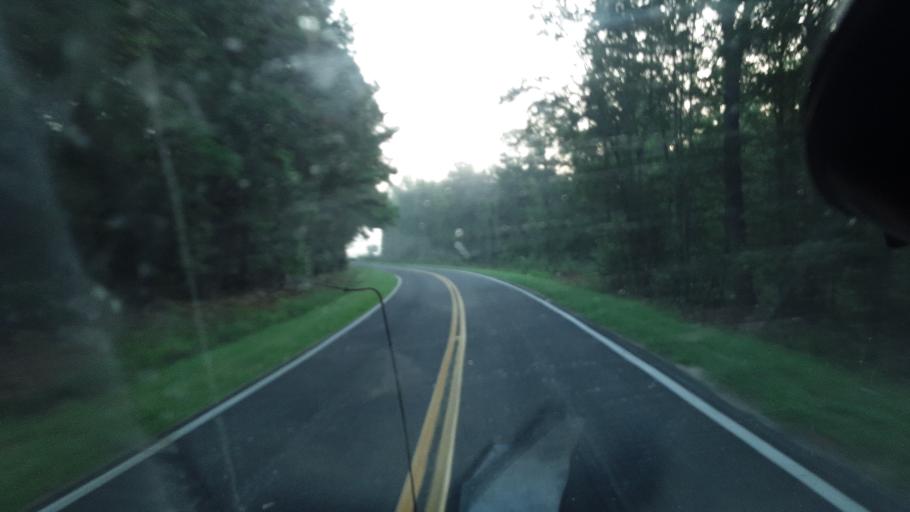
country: US
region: South Carolina
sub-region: Clarendon County
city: Manning
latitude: 33.7146
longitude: -80.1380
